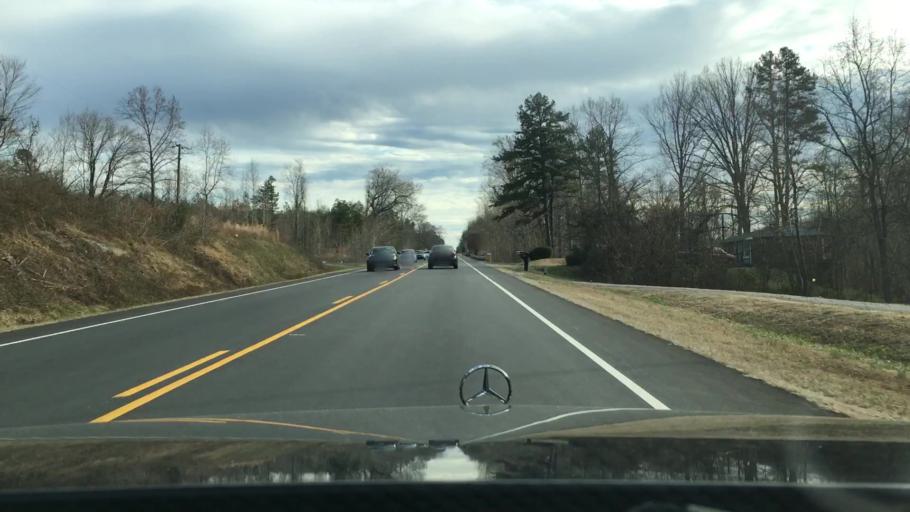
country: US
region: North Carolina
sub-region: Caswell County
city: Yanceyville
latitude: 36.4596
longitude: -79.3716
